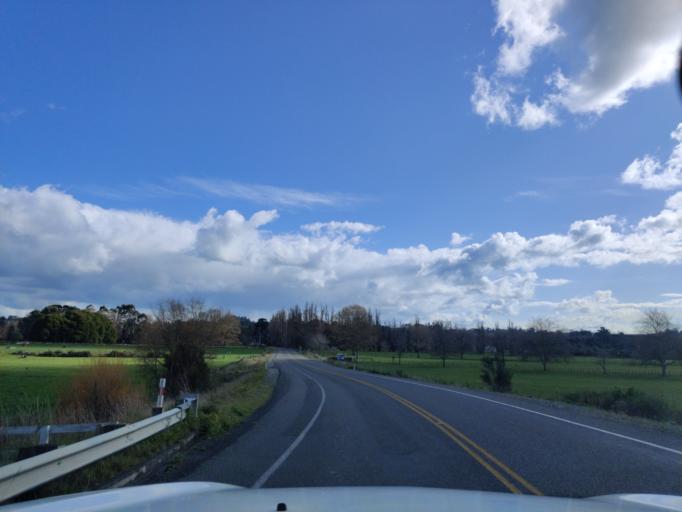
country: NZ
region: Manawatu-Wanganui
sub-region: Palmerston North City
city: Palmerston North
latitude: -40.2809
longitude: 175.7699
